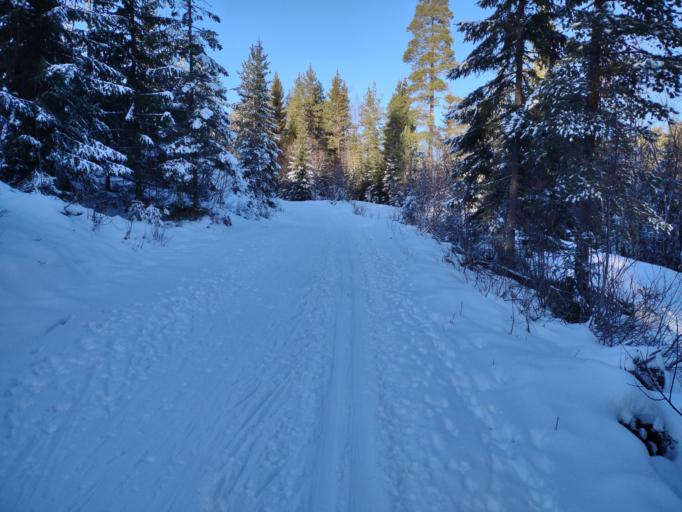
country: NO
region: Buskerud
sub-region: Kongsberg
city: Kongsberg
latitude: 59.6689
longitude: 9.6170
